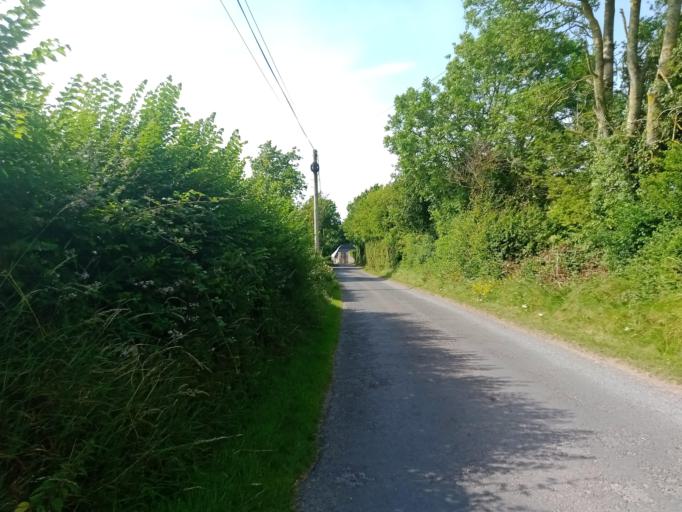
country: IE
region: Leinster
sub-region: Laois
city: Rathdowney
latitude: 52.8147
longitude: -7.4717
